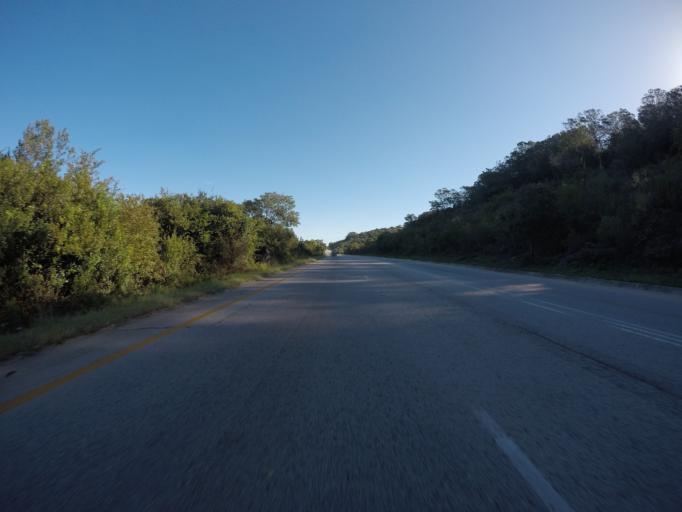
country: ZA
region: Eastern Cape
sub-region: Cacadu District Municipality
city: Jeffrey's Bay
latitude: -33.9035
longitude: 25.0813
